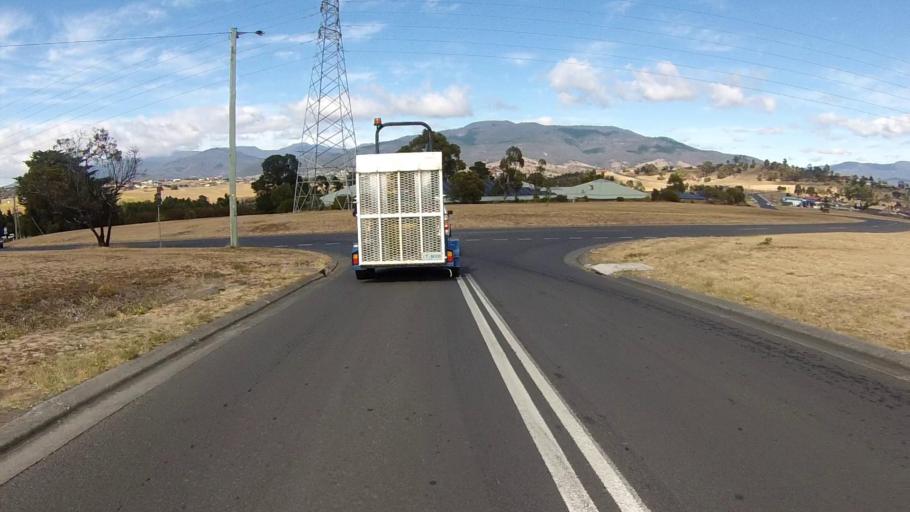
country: AU
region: Tasmania
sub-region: Brighton
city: Old Beach
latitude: -42.7504
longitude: 147.2795
